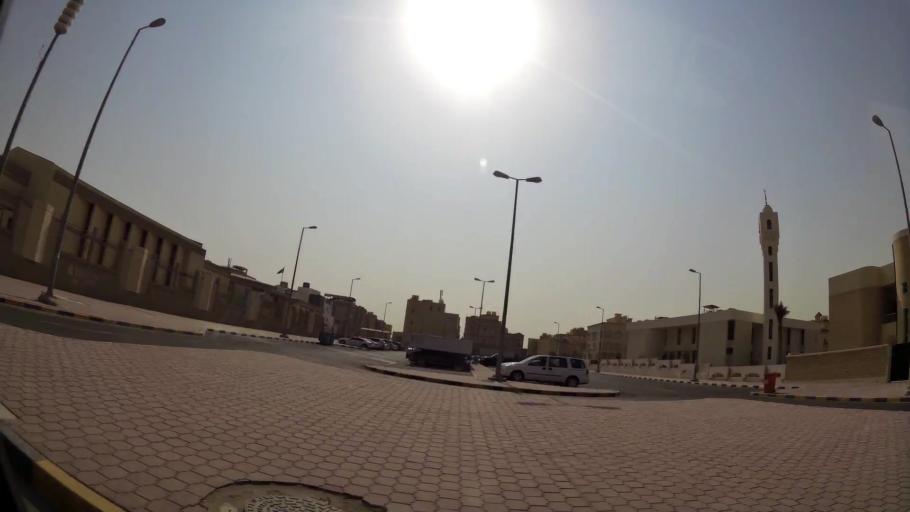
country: KW
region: Muhafazat al Jahra'
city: Al Jahra'
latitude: 29.3374
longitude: 47.7664
